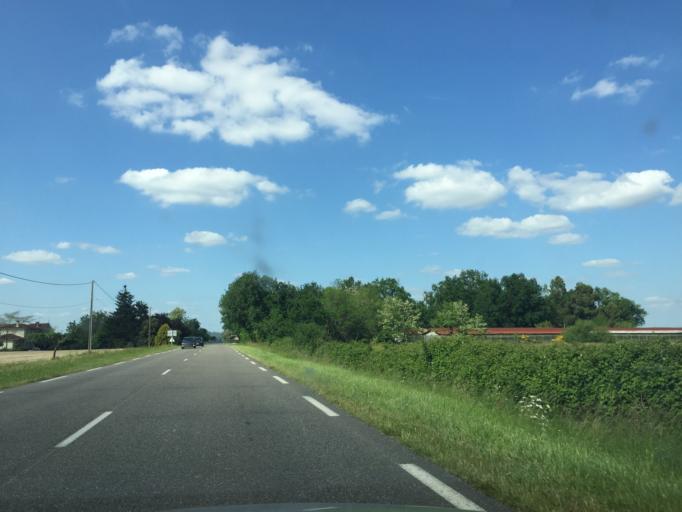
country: FR
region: Aquitaine
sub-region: Departement de la Gironde
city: La Reole
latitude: 44.5227
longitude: -0.0463
